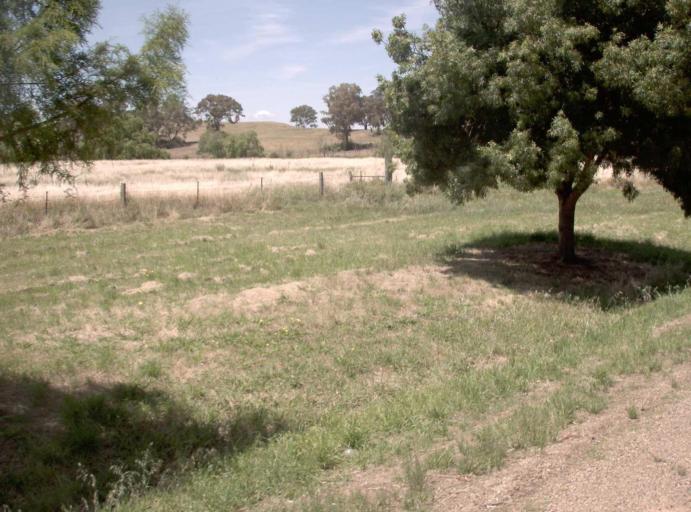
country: AU
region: Victoria
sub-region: East Gippsland
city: Bairnsdale
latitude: -37.2519
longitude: 147.7119
